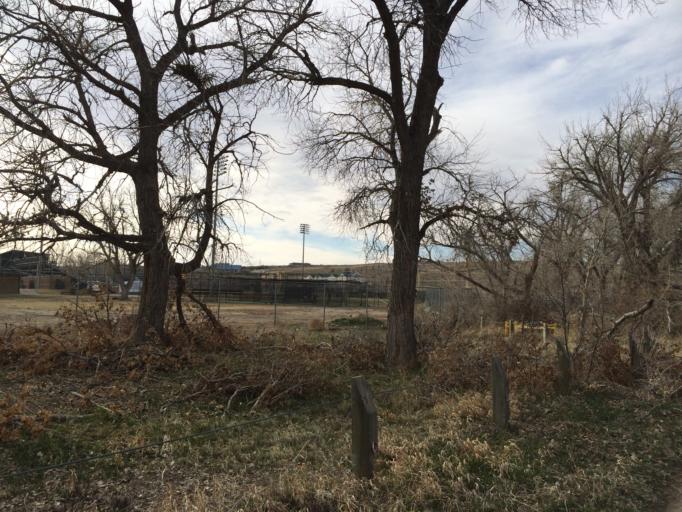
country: US
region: Wyoming
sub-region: Natrona County
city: Casper
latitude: 42.8595
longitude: -106.3280
